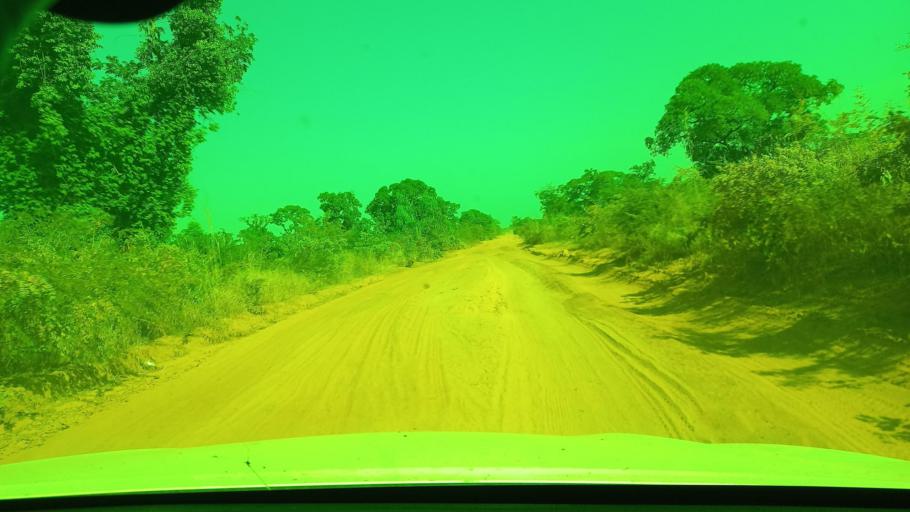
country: ML
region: Bamako
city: Bamako
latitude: 12.3973
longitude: -7.9913
